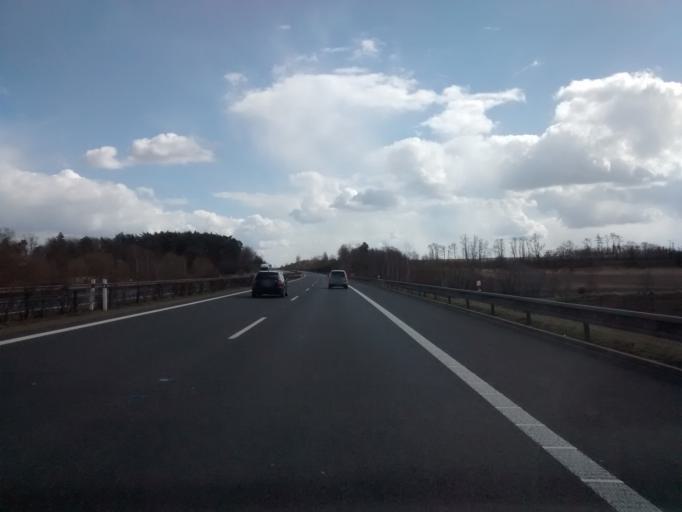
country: CZ
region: Ustecky
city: Roudnice nad Labem
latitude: 50.3726
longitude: 14.2520
